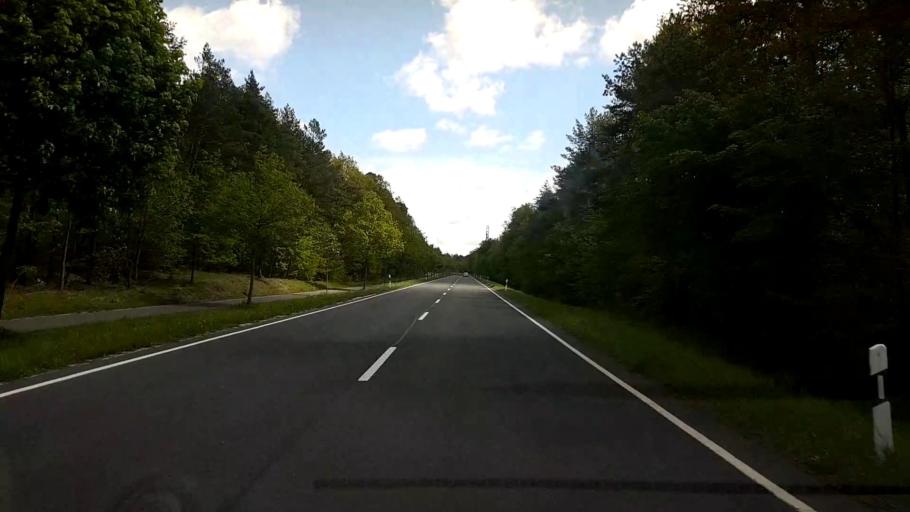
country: DE
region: Bavaria
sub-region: Upper Franconia
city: Bamberg
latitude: 49.8888
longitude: 10.9384
